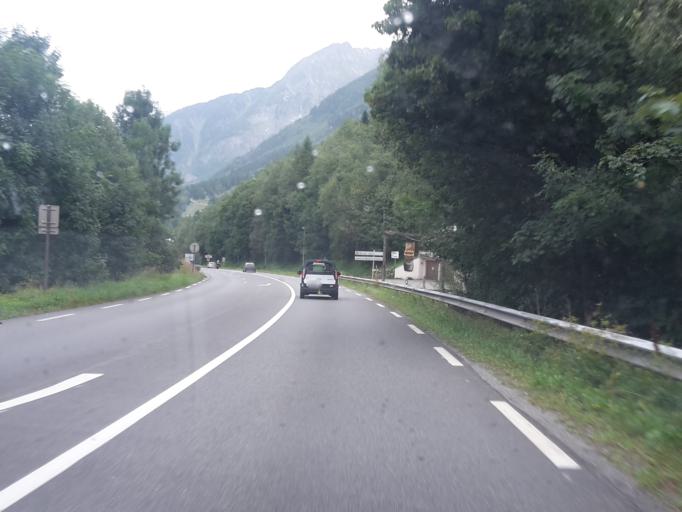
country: FR
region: Rhone-Alpes
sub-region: Departement de la Haute-Savoie
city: Chamonix-Mont-Blanc
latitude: 45.9127
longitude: 6.8641
